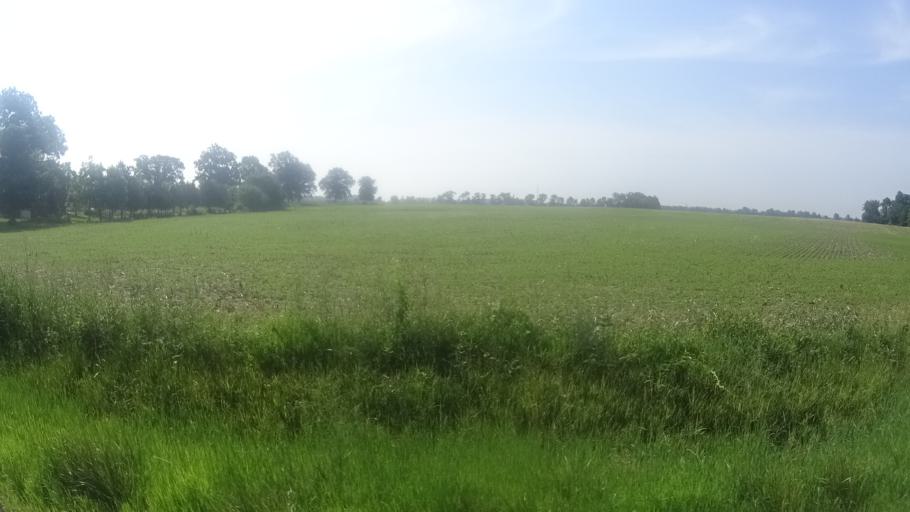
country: US
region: Ohio
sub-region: Huron County
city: Bellevue
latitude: 41.2873
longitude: -82.7797
